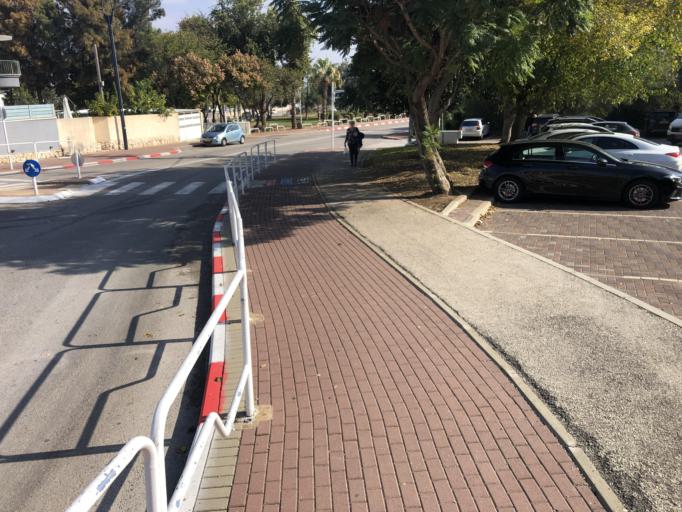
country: IL
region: Northern District
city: `Akko
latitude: 32.9331
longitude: 35.0915
